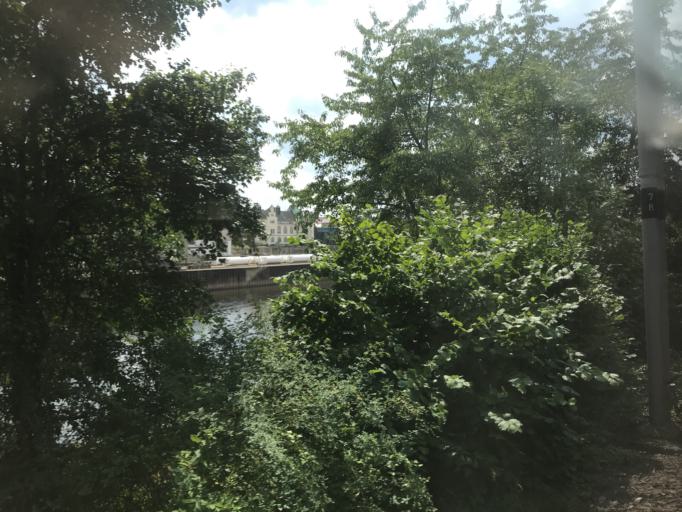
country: CZ
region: Ustecky
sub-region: Okres Decin
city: Decin
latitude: 50.7881
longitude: 14.2207
